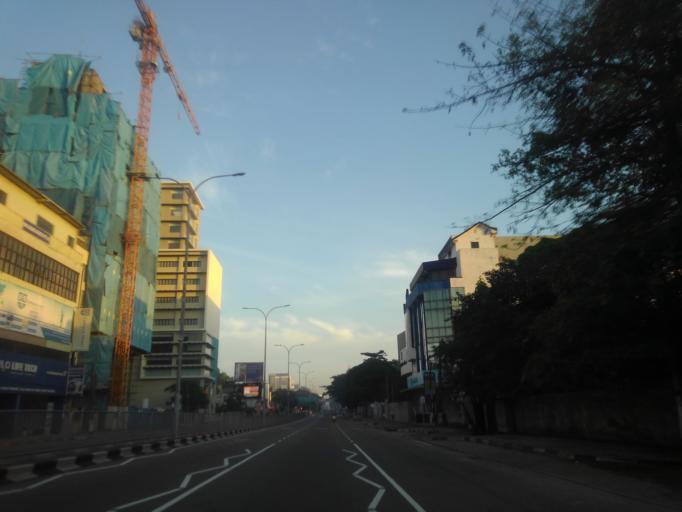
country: LK
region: Western
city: Pita Kotte
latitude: 6.9051
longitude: 79.8774
